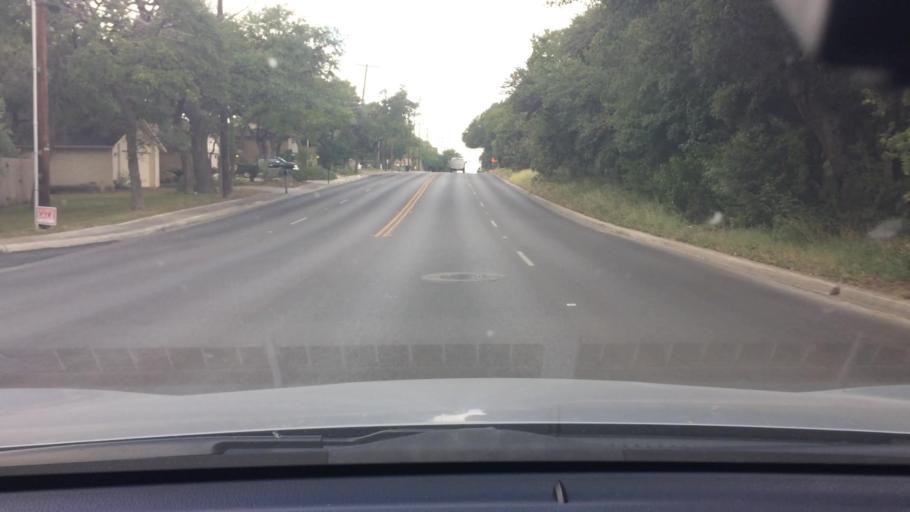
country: US
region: Texas
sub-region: Bexar County
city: Hollywood Park
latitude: 29.5588
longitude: -98.4747
